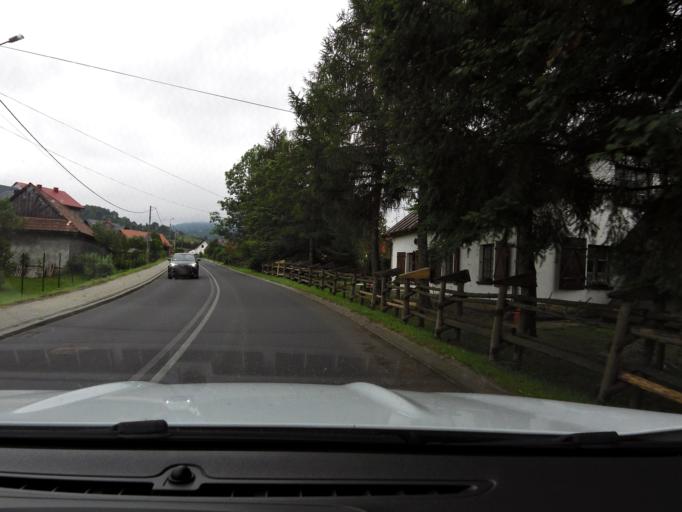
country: PL
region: Silesian Voivodeship
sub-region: Powiat zywiecki
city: Ujsoly
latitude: 49.4846
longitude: 19.1328
